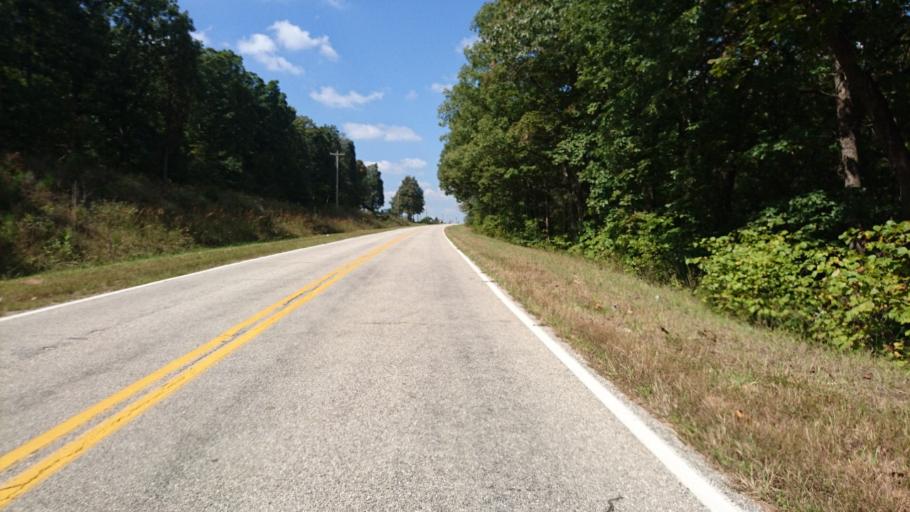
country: US
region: Missouri
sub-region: Pulaski County
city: Richland
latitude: 37.7527
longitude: -92.5021
